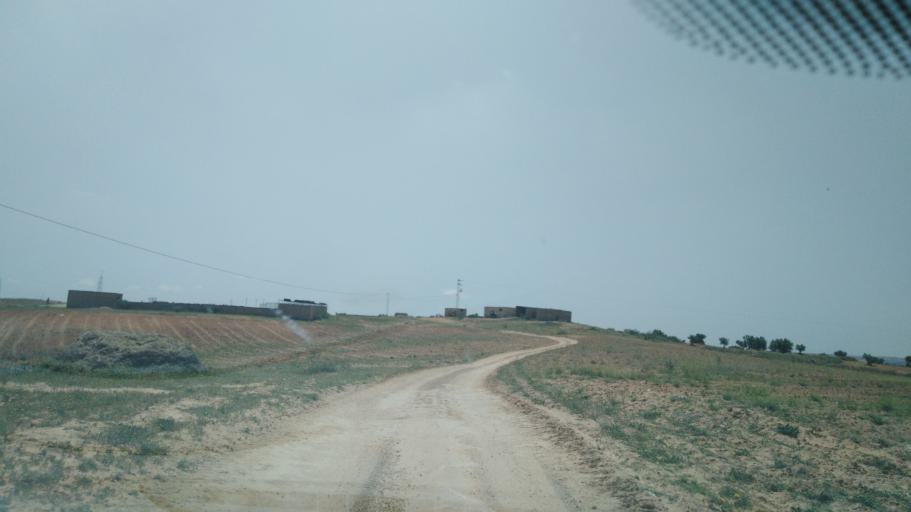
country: TN
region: Safaqis
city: Sfax
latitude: 34.7697
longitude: 10.5782
